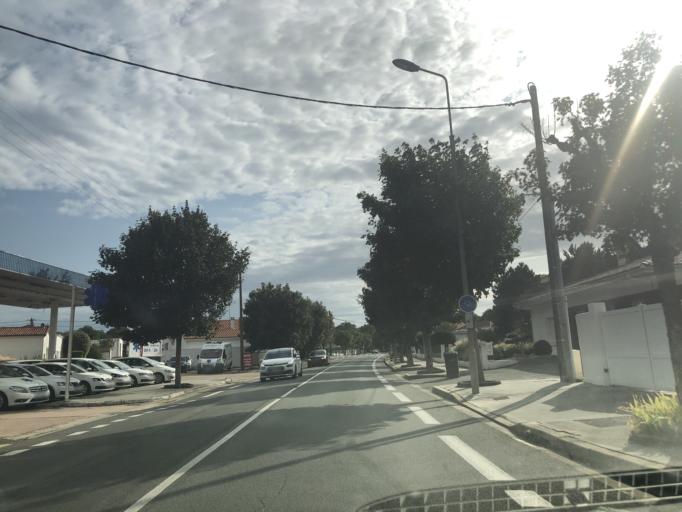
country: FR
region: Poitou-Charentes
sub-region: Departement de la Charente-Maritime
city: Royan
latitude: 45.6292
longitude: -1.0396
